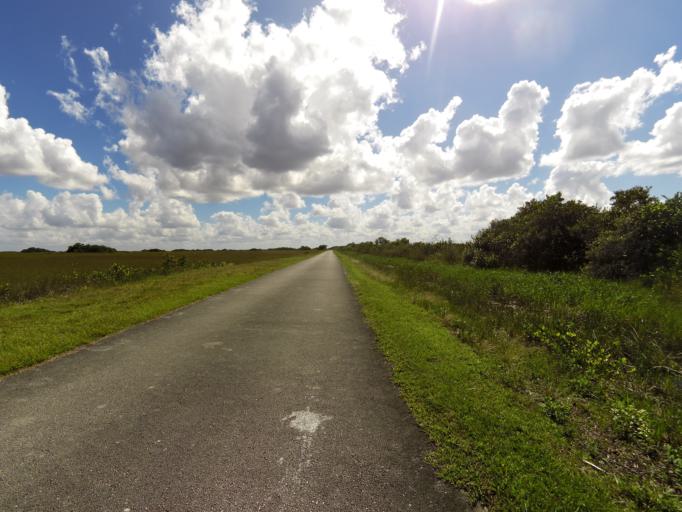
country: US
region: Florida
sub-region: Miami-Dade County
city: The Hammocks
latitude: 25.6953
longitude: -80.7669
